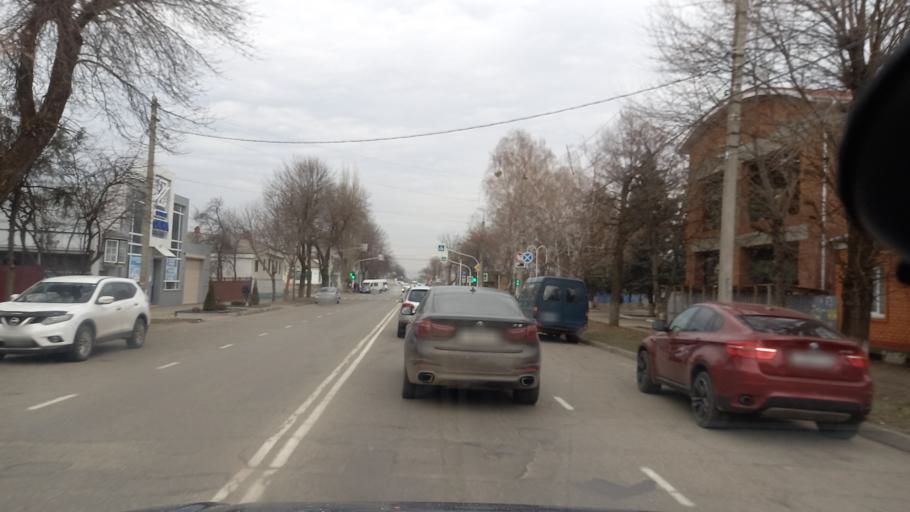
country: RU
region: Adygeya
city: Maykop
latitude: 44.6061
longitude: 40.1114
